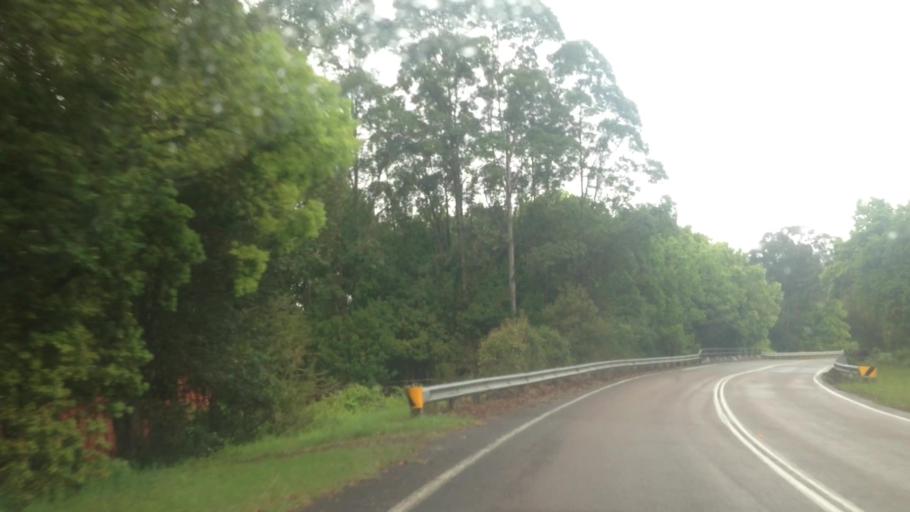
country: AU
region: New South Wales
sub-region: Wyong Shire
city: Little Jilliby
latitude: -33.2362
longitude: 151.3788
